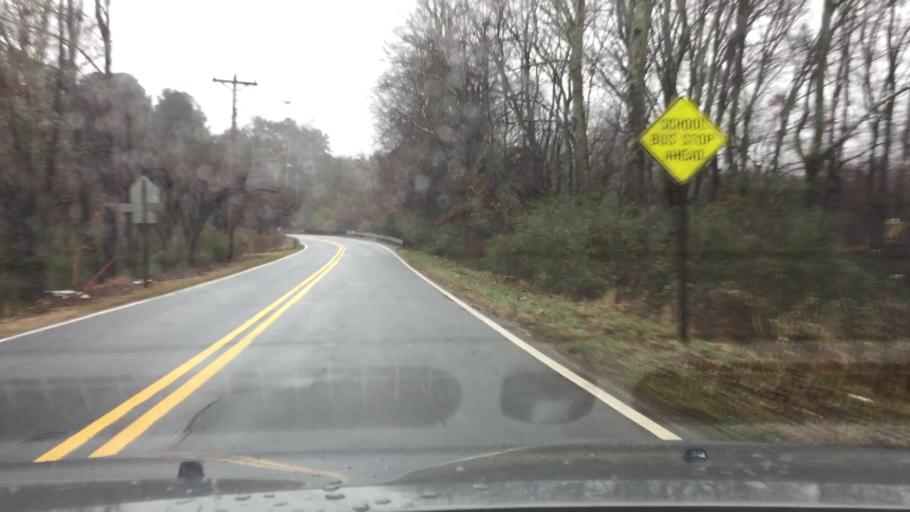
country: US
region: Georgia
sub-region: Cobb County
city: Fair Oaks
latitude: 33.9174
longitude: -84.6186
